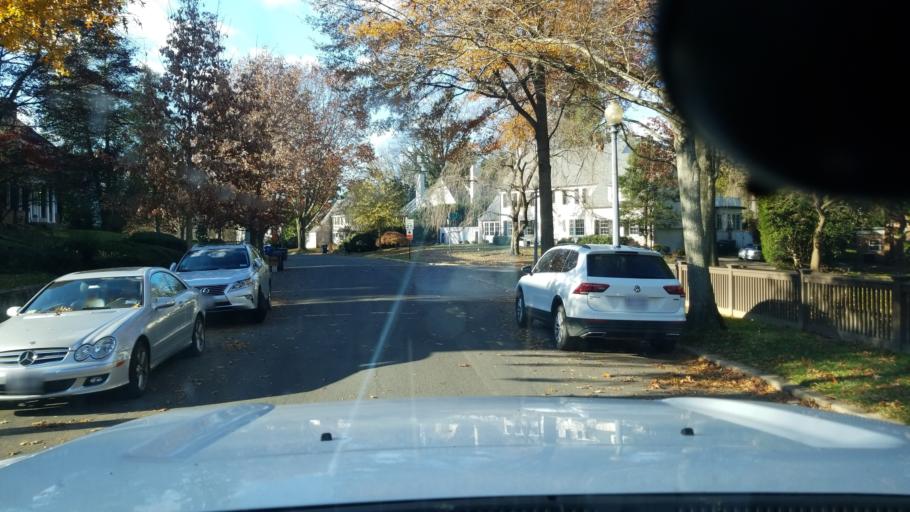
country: US
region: Maryland
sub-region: Montgomery County
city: Brookmont
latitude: 38.9407
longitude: -77.1005
